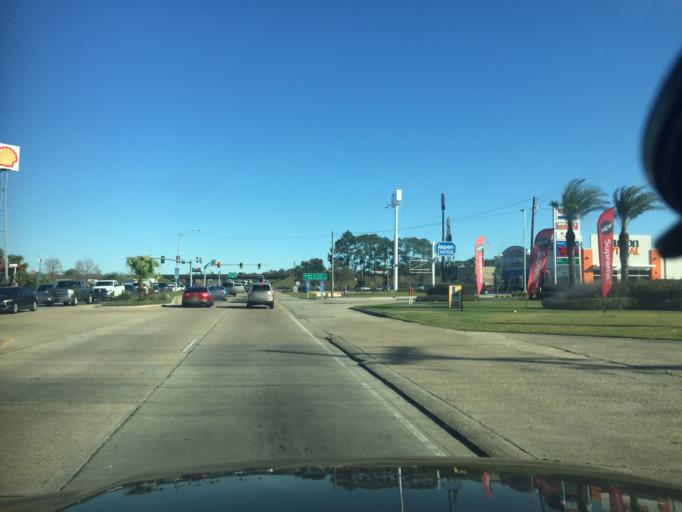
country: US
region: Louisiana
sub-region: Saint Tammany Parish
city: Slidell
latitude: 30.2847
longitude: -89.7527
